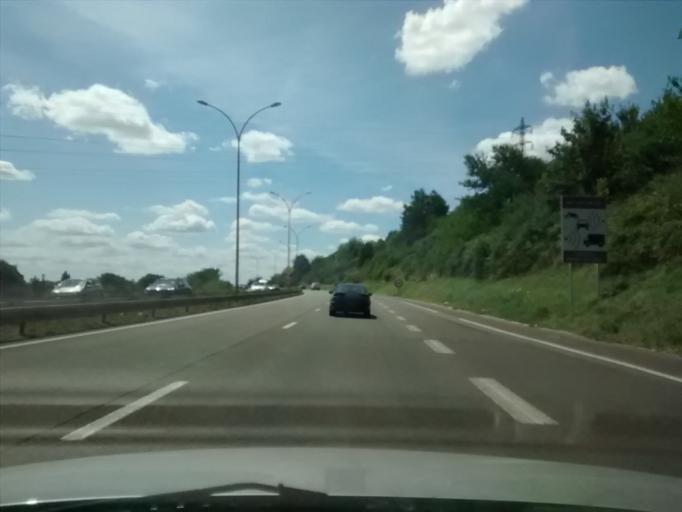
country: FR
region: Pays de la Loire
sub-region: Departement de la Sarthe
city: Le Mans
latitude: 48.0003
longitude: 0.1727
